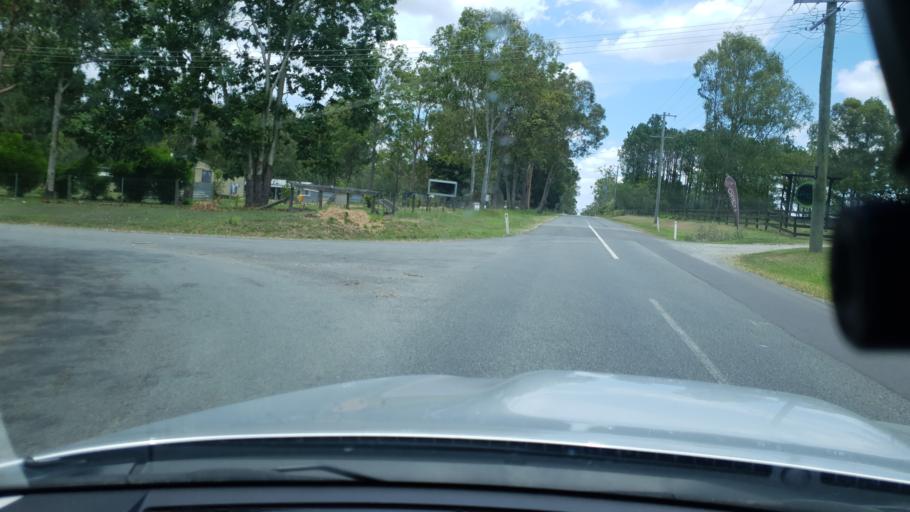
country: AU
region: Queensland
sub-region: Logan
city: North Maclean
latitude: -27.7724
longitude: 152.9922
